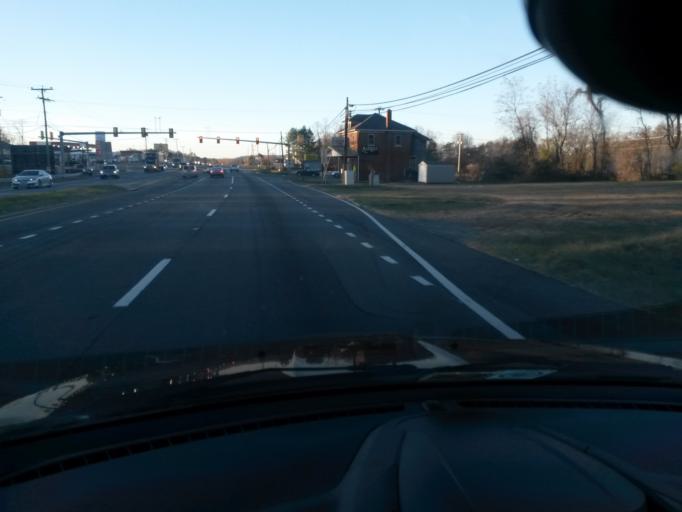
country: US
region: Virginia
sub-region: Franklin County
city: Henry Fork
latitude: 36.9568
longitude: -79.8790
